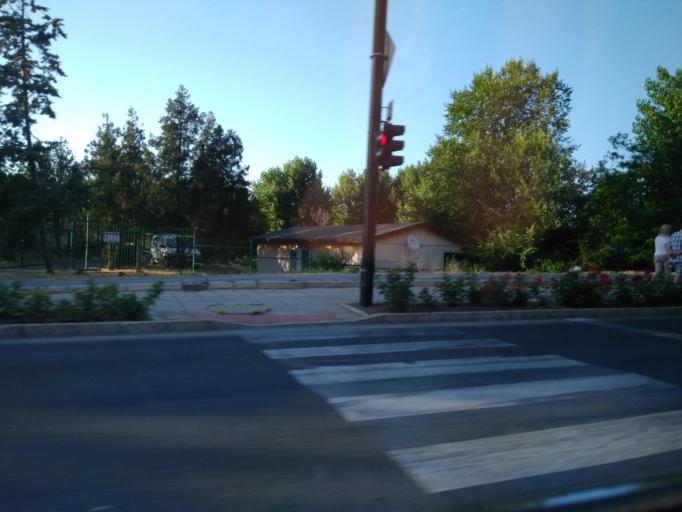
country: BG
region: Burgas
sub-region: Obshtina Nesebur
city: Nesebar
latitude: 42.6652
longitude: 27.7132
